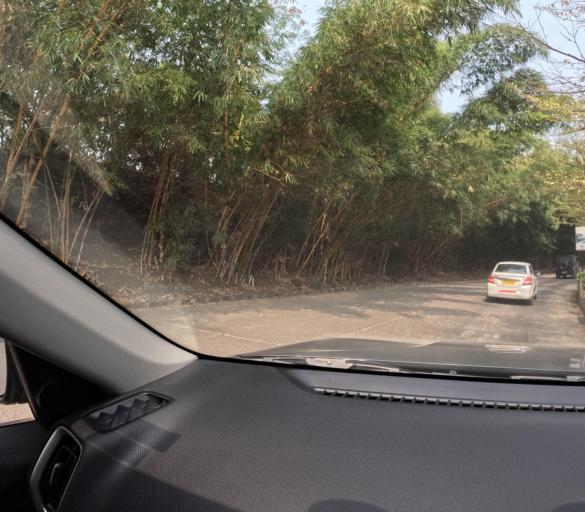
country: IN
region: Maharashtra
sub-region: Pune Division
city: Kharakvasla
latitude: 18.5042
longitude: 73.7386
